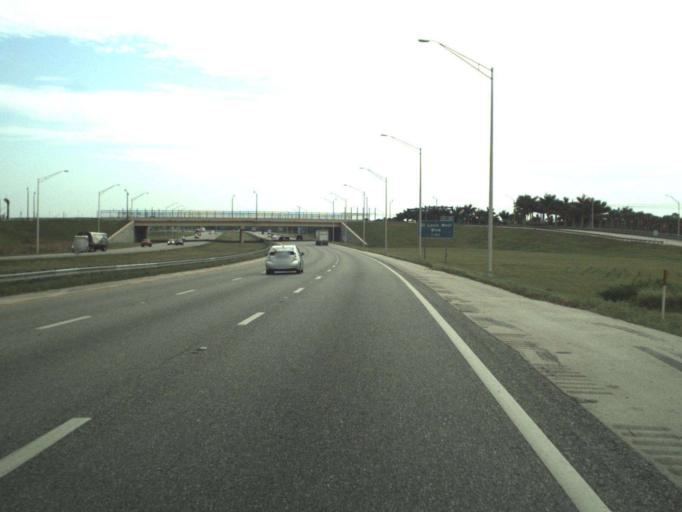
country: US
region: Florida
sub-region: Saint Lucie County
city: Port Saint Lucie
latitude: 27.2912
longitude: -80.4192
